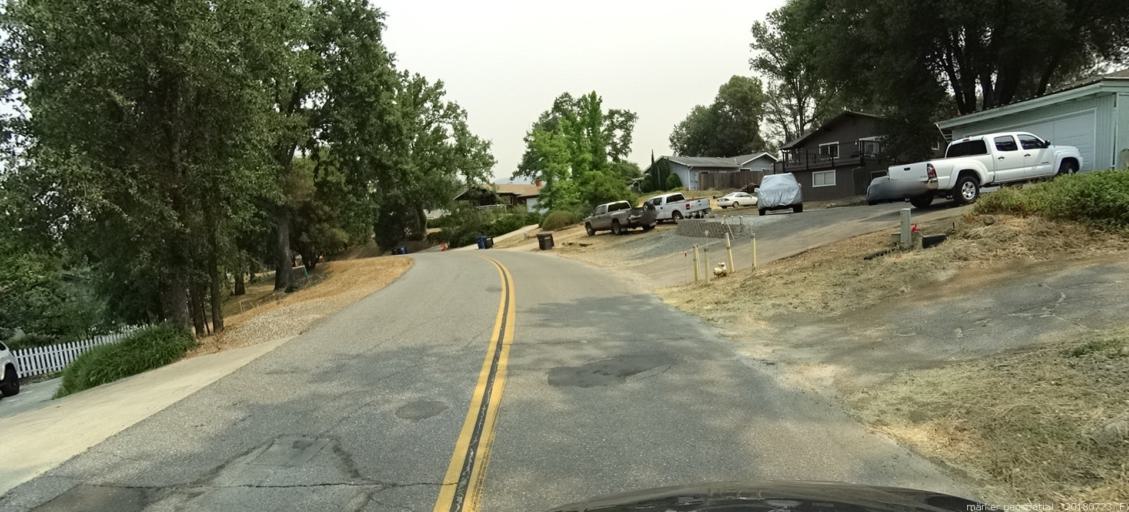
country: US
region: California
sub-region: Madera County
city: Ahwahnee
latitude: 37.3412
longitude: -119.7101
